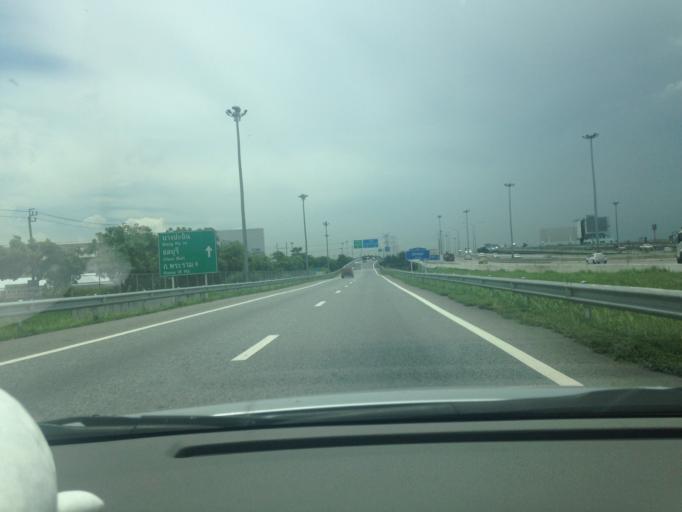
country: TH
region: Bangkok
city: Suan Luang
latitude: 13.7177
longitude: 100.7001
